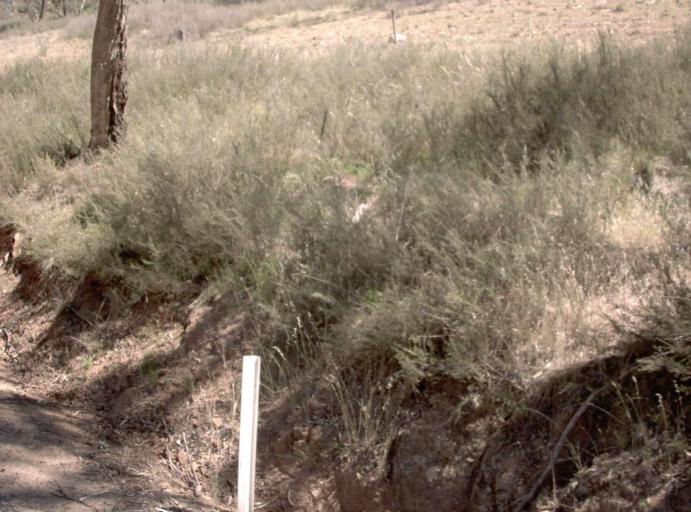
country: AU
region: New South Wales
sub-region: Snowy River
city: Jindabyne
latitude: -37.0606
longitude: 148.5735
